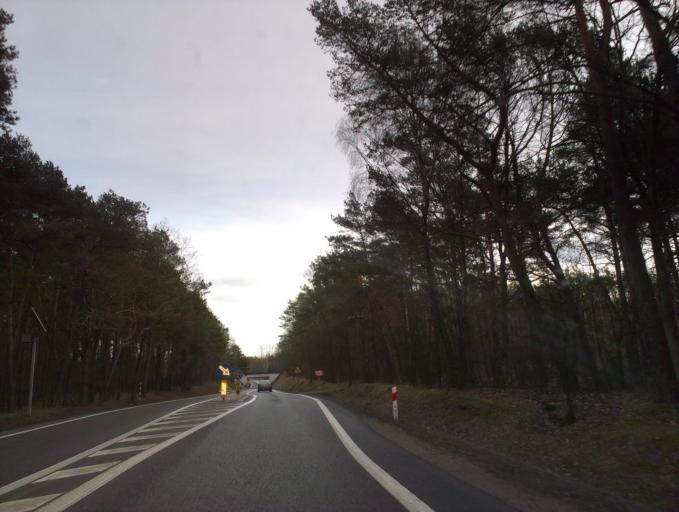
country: PL
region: Masovian Voivodeship
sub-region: Powiat sierpecki
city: Sierpc
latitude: 52.8699
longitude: 19.6260
